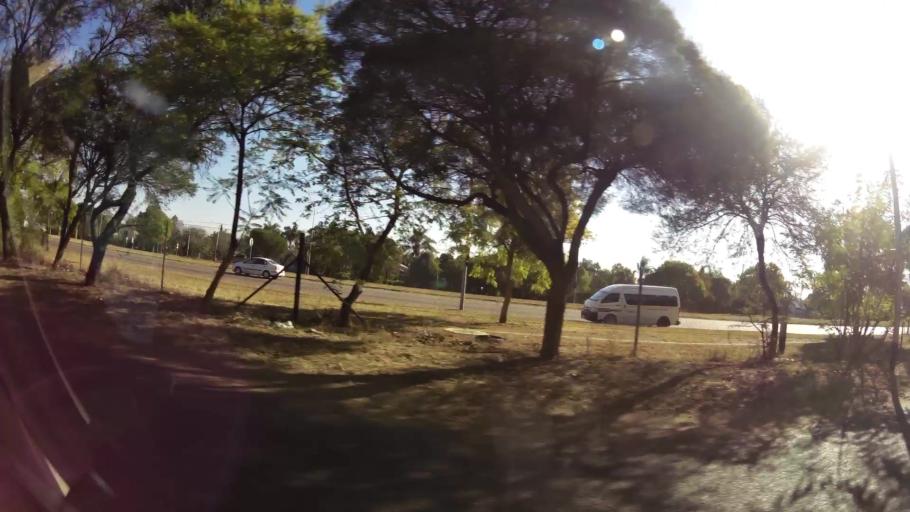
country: ZA
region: Gauteng
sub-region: City of Tshwane Metropolitan Municipality
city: Pretoria
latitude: -25.7159
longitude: 28.2581
